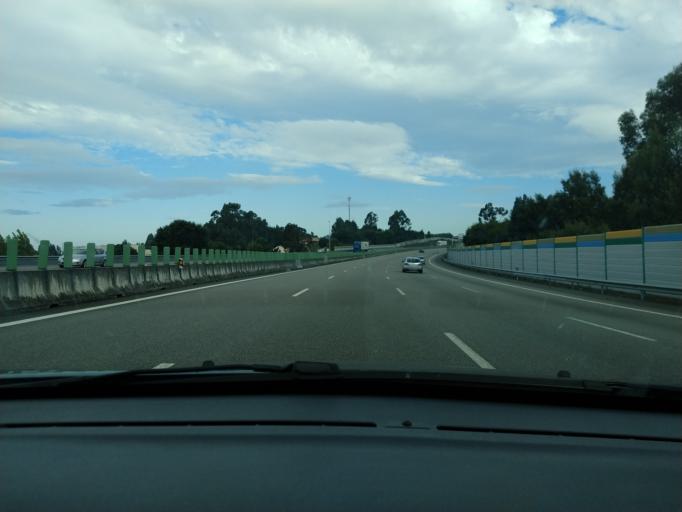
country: PT
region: Porto
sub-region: Vila Nova de Gaia
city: Grijo
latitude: 41.0328
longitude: -8.5720
